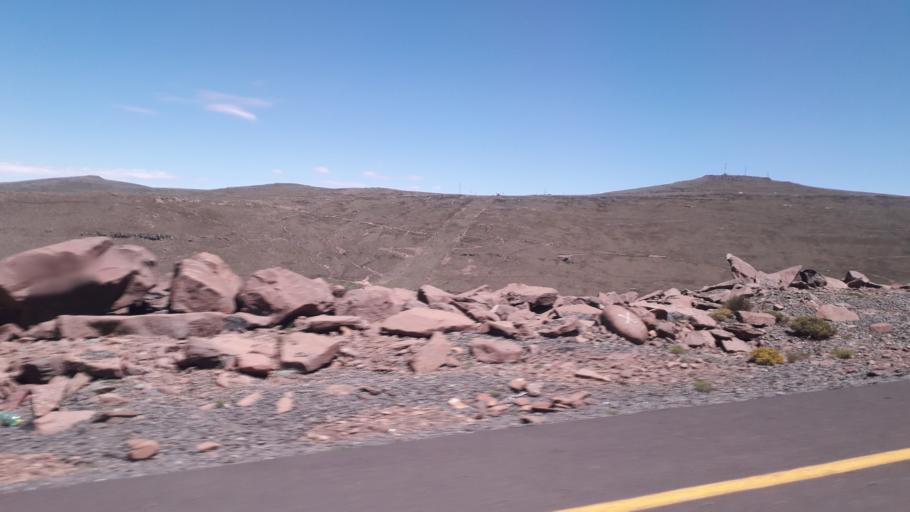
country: ZA
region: Orange Free State
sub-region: Thabo Mofutsanyana District Municipality
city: Phuthaditjhaba
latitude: -28.8253
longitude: 28.7327
